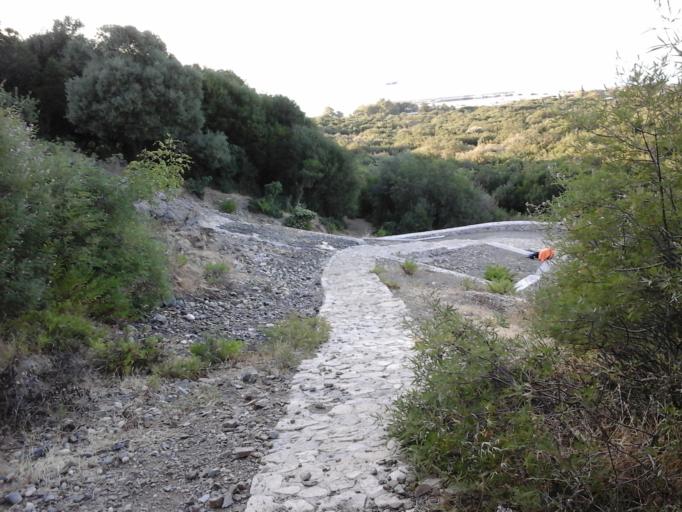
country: GR
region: East Macedonia and Thrace
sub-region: Nomos Evrou
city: Samothraki
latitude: 40.4985
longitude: 25.6024
